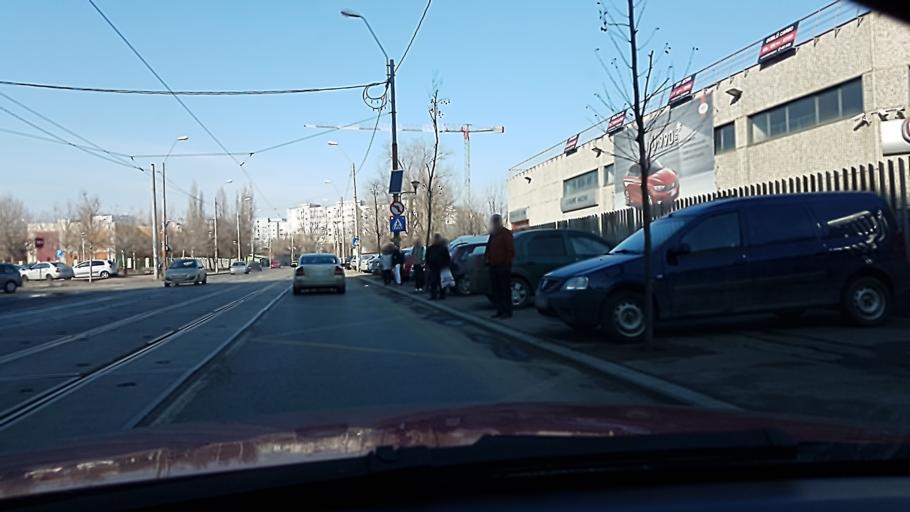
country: RO
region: Ilfov
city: Dobroesti
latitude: 44.4322
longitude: 26.1728
